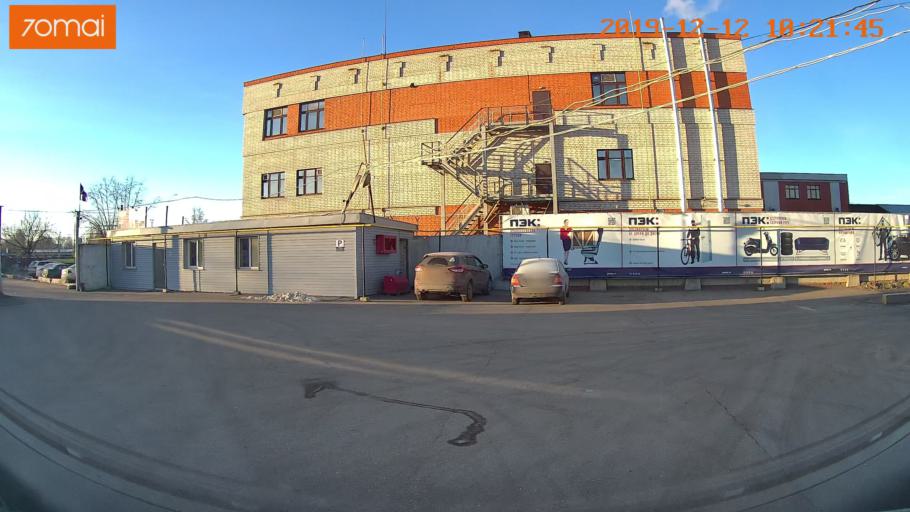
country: RU
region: Ivanovo
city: Novo-Talitsy
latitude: 56.9990
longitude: 40.9151
